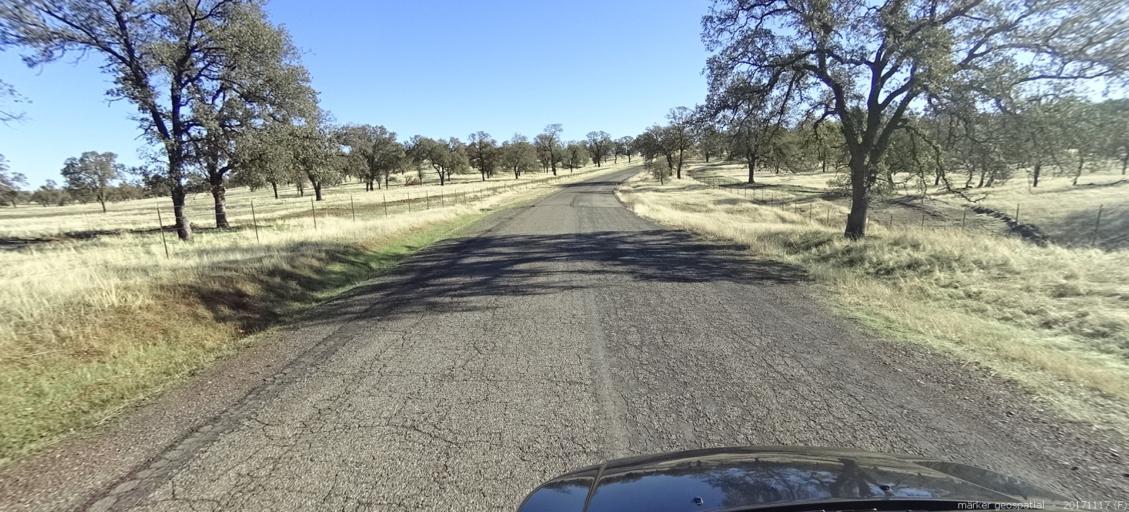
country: US
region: California
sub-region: Shasta County
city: Cottonwood
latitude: 40.4253
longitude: -122.1823
